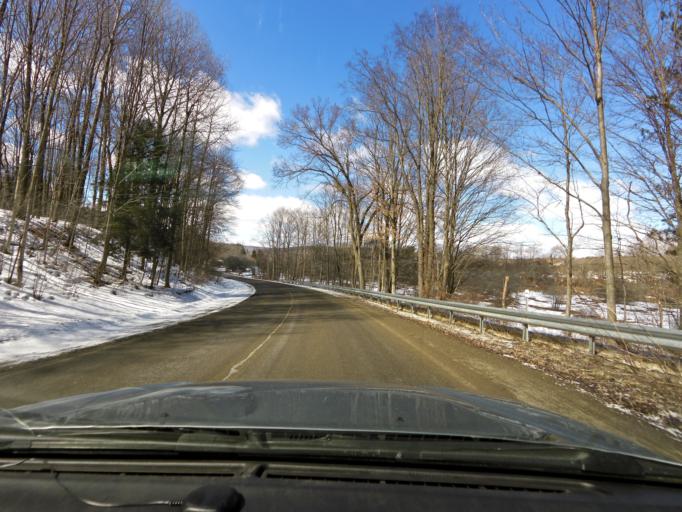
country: US
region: New York
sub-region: Cattaraugus County
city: Franklinville
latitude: 42.3441
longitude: -78.4375
